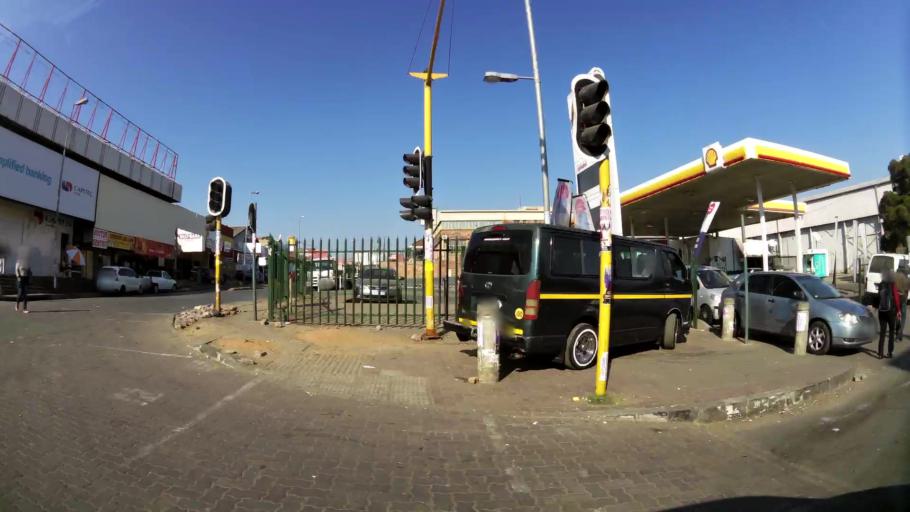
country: ZA
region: Gauteng
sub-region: City of Johannesburg Metropolitan Municipality
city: Modderfontein
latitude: -26.1103
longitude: 28.0866
